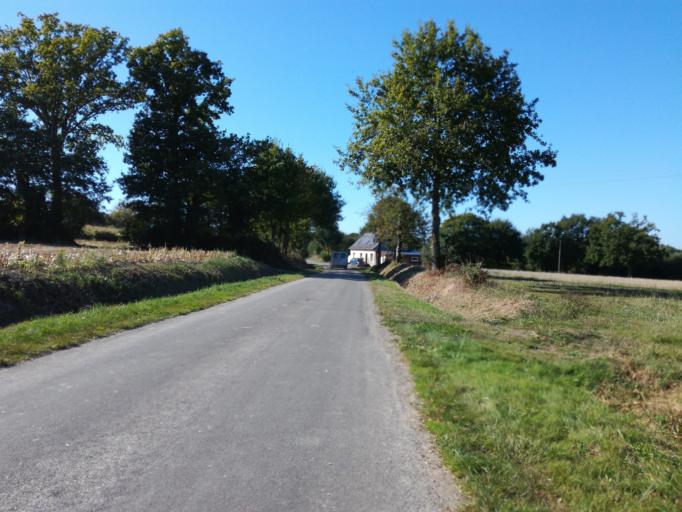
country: FR
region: Brittany
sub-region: Departement d'Ille-et-Vilaine
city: Saint-Jean-sur-Couesnon
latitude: 48.2618
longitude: -1.3717
